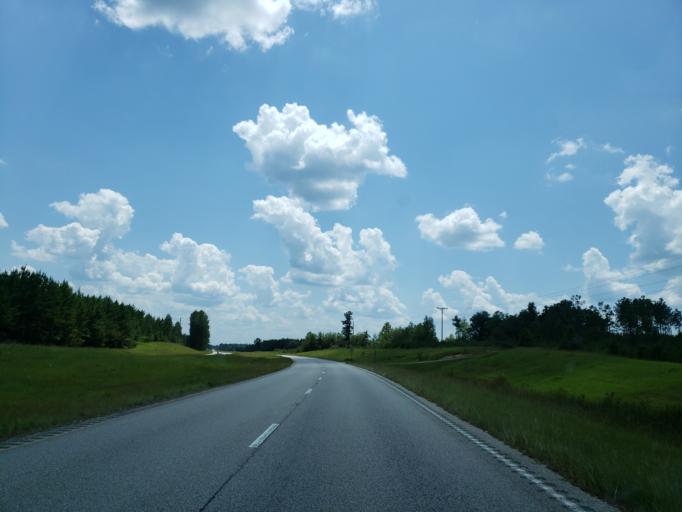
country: US
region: Mississippi
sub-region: Wayne County
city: Belmont
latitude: 31.3916
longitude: -88.4778
